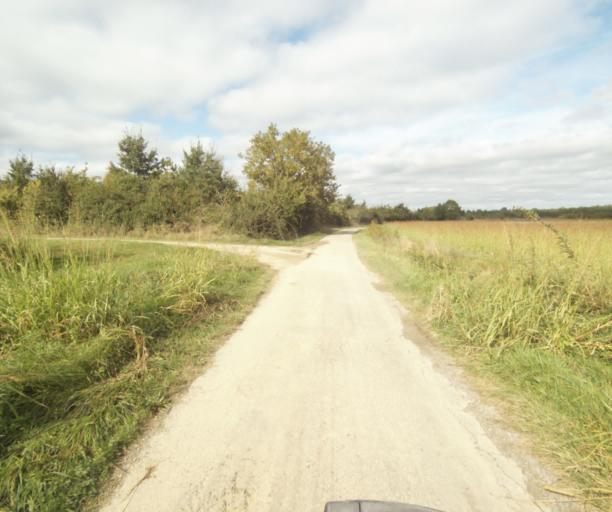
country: FR
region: Midi-Pyrenees
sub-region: Departement du Tarn-et-Garonne
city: Finhan
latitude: 43.9207
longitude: 1.2081
